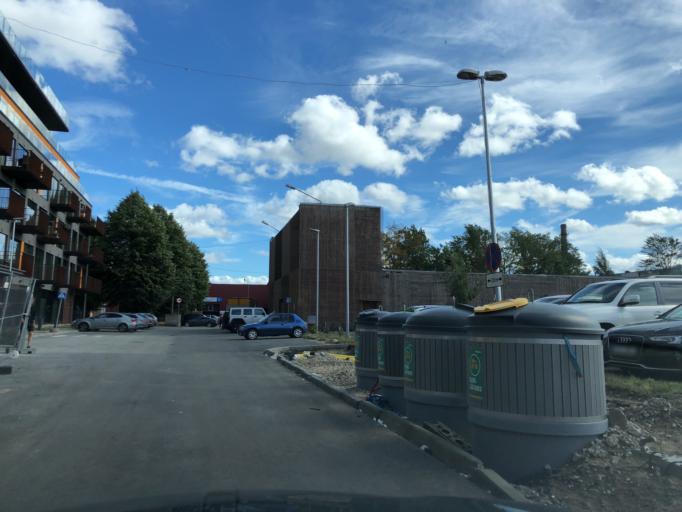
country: EE
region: Harju
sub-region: Tallinna linn
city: Tallinn
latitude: 59.4494
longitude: 24.7236
